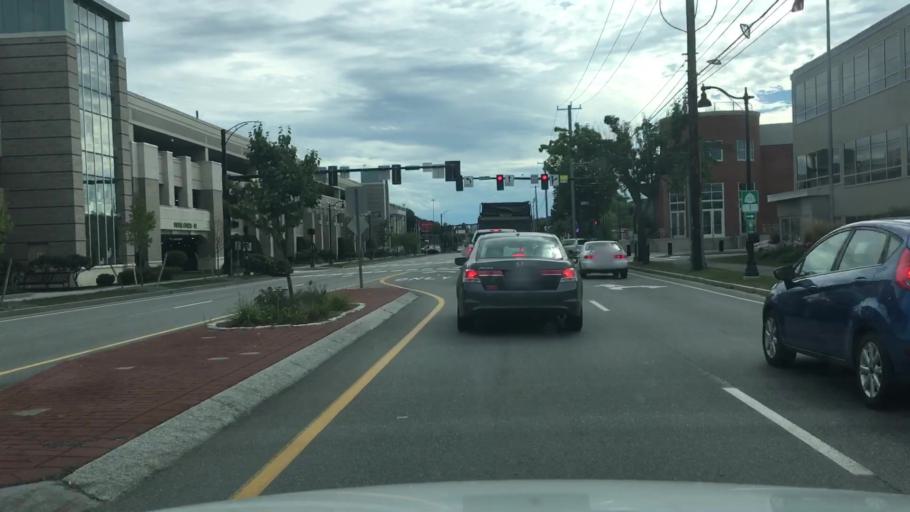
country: US
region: Maine
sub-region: Penobscot County
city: Bangor
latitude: 44.7900
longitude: -68.7773
